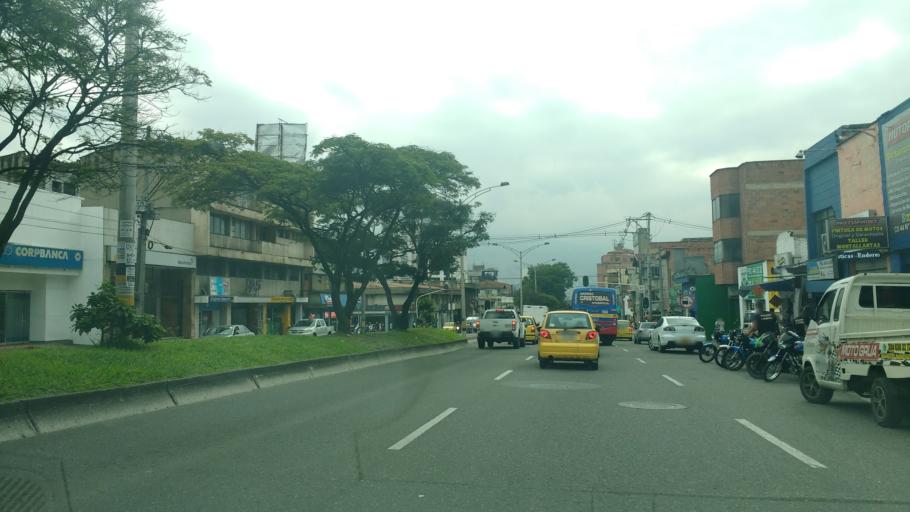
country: CO
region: Antioquia
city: Medellin
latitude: 6.2497
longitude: -75.5929
